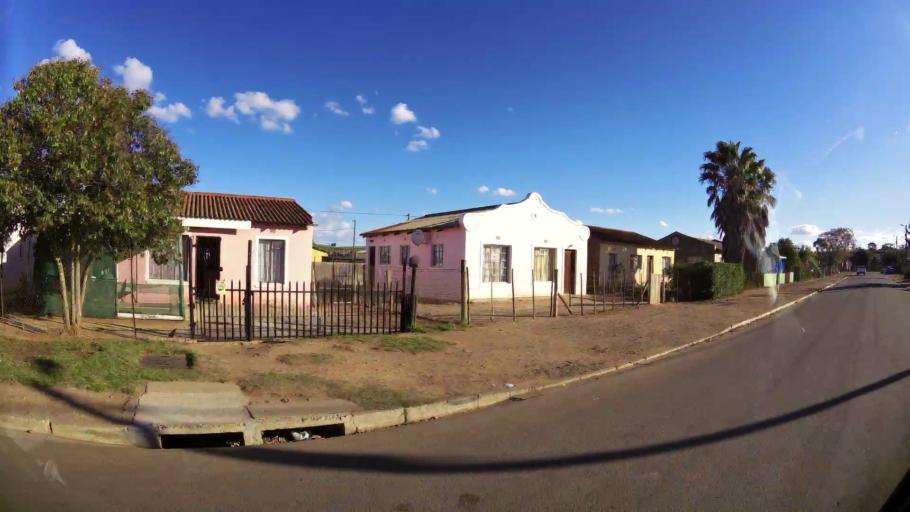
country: ZA
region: Western Cape
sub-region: Eden District Municipality
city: Riversdale
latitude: -34.1056
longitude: 20.9634
